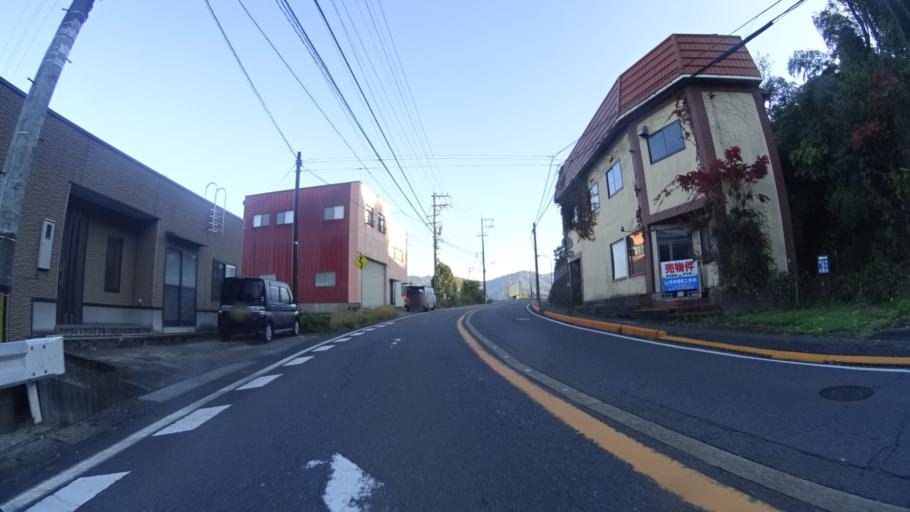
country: JP
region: Fukui
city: Maruoka
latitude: 36.0936
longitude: 136.3027
